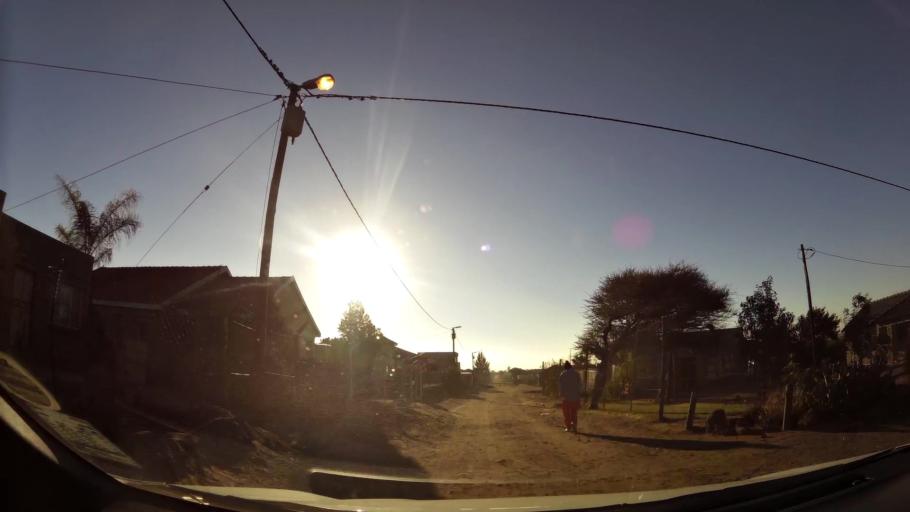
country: ZA
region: Limpopo
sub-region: Capricorn District Municipality
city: Polokwane
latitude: -23.8398
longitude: 29.3541
